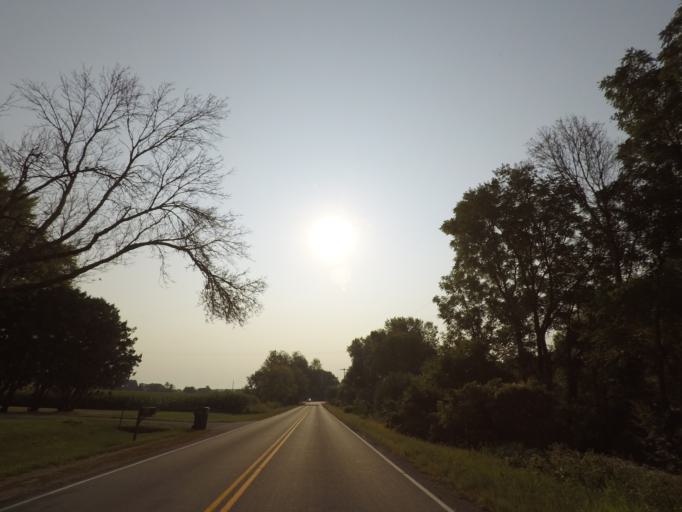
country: US
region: Wisconsin
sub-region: Dane County
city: Cottage Grove
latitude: 43.0518
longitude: -89.2490
